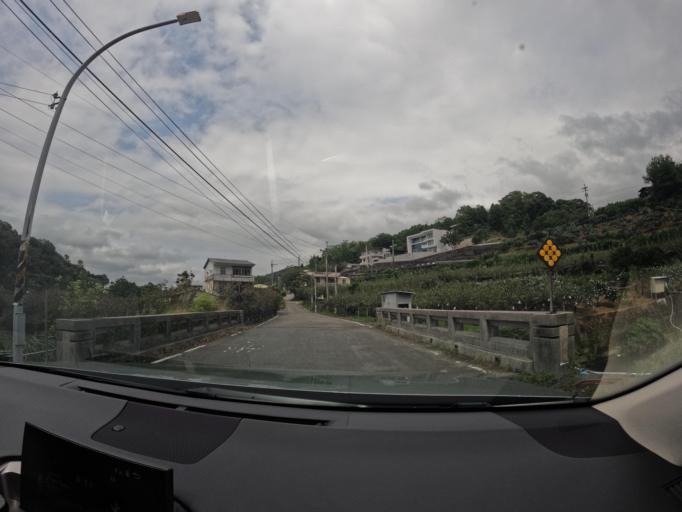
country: TW
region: Taiwan
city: Fengyuan
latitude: 24.3380
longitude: 120.8745
